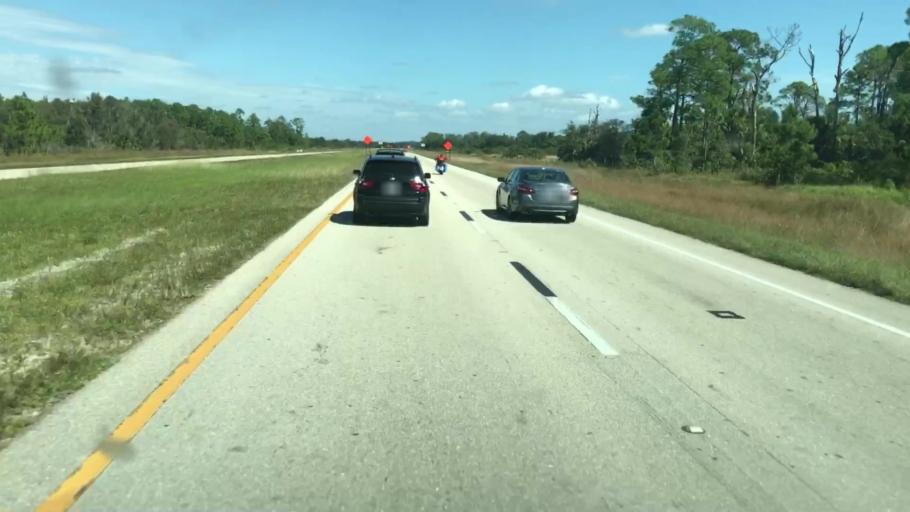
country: US
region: Florida
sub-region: Lee County
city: Gateway
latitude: 26.5676
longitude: -81.7295
